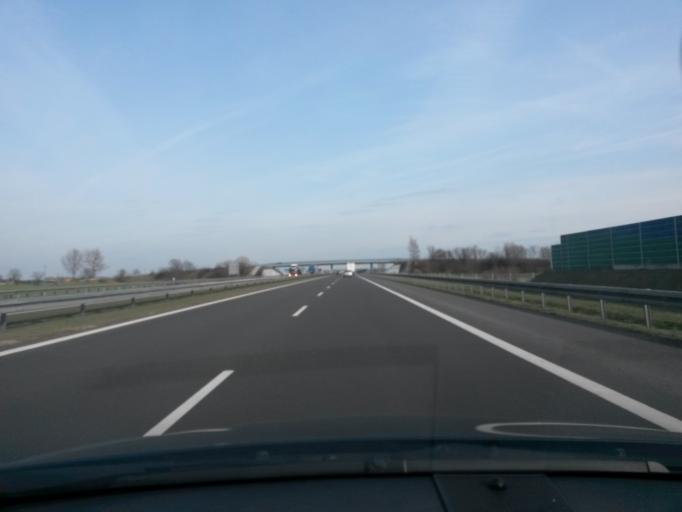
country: PL
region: Greater Poland Voivodeship
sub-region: Powiat slupecki
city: Strzalkowo
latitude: 52.2595
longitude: 17.7901
